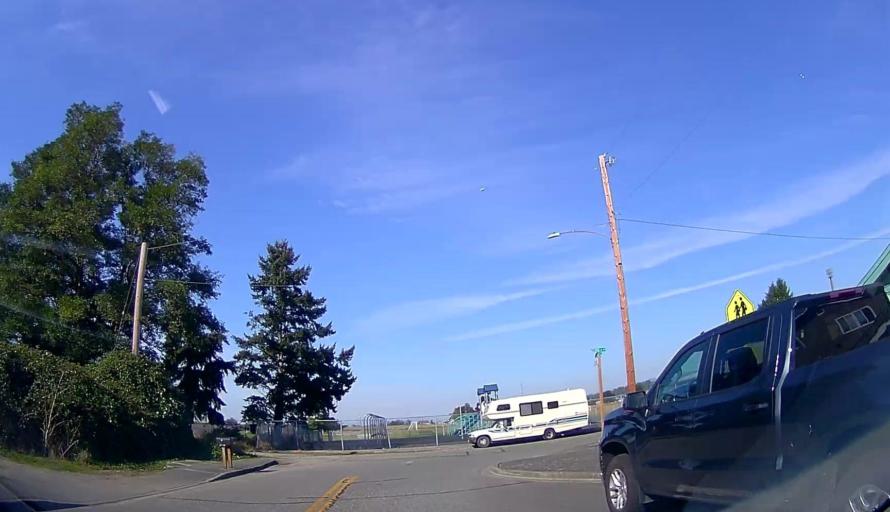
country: US
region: Washington
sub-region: Snohomish County
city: Stanwood
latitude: 48.2444
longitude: -122.3741
